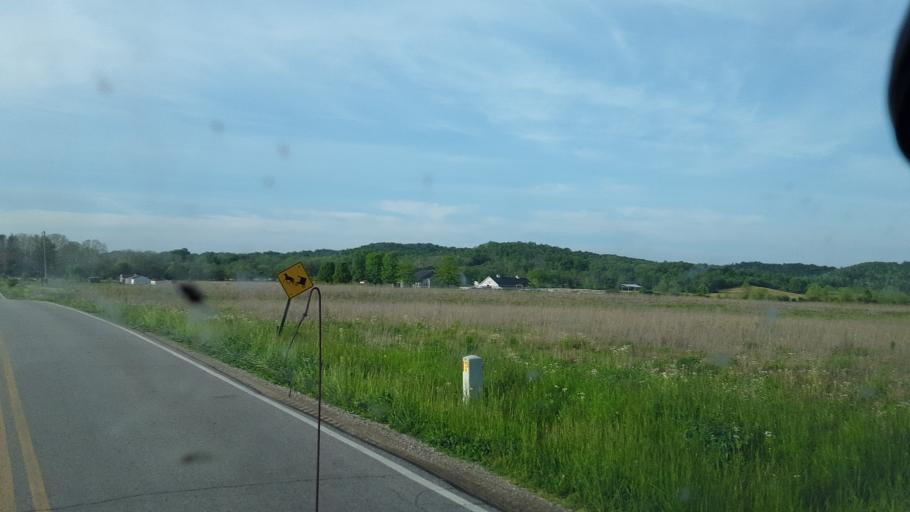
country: US
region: Ohio
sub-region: Ross County
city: Kingston
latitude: 39.4969
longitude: -82.7002
